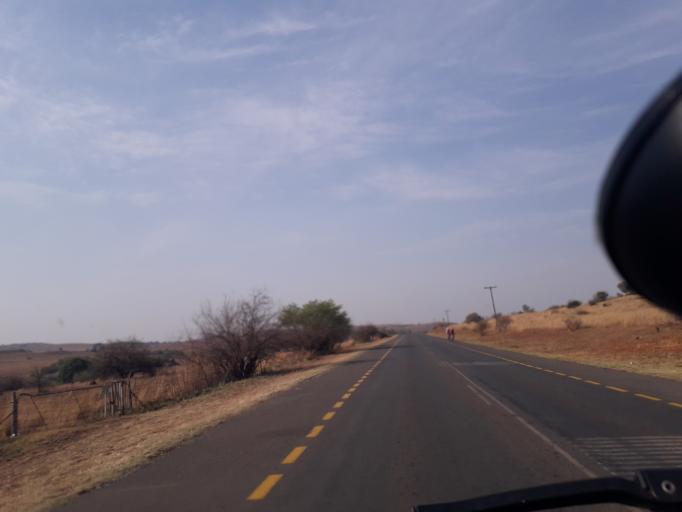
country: ZA
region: Gauteng
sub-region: West Rand District Municipality
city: Krugersdorp
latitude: -26.0209
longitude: 27.7255
